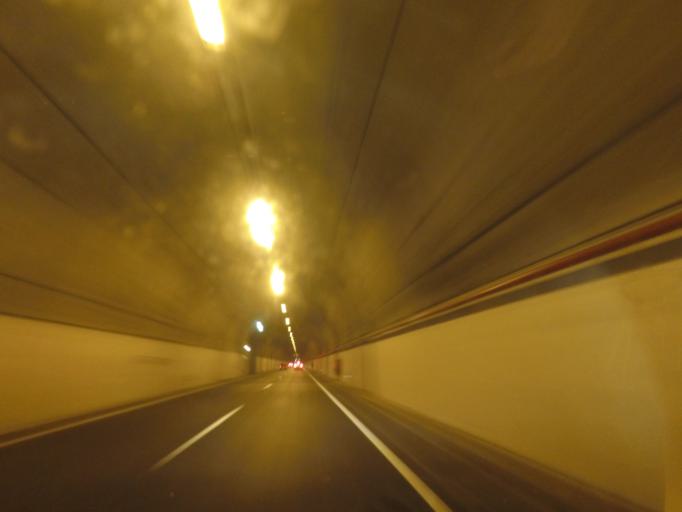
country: PT
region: Madeira
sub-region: Ribeira Brava
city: Campanario
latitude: 32.6595
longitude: -17.0065
